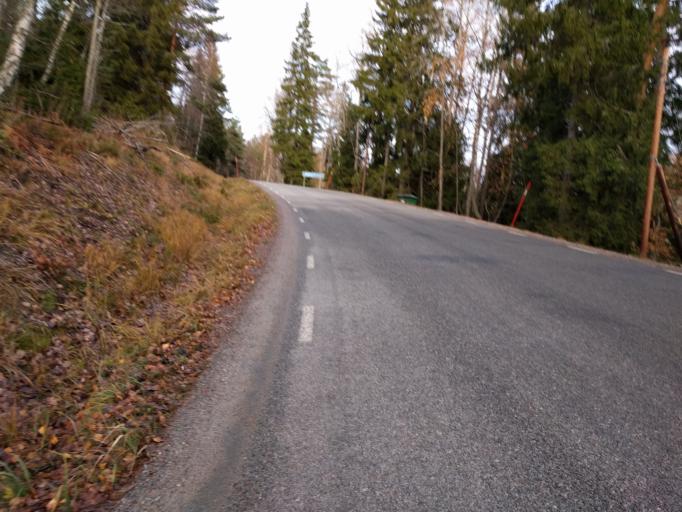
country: SE
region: Stockholm
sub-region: Osterakers Kommun
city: Akersberga
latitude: 59.5934
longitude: 18.3453
